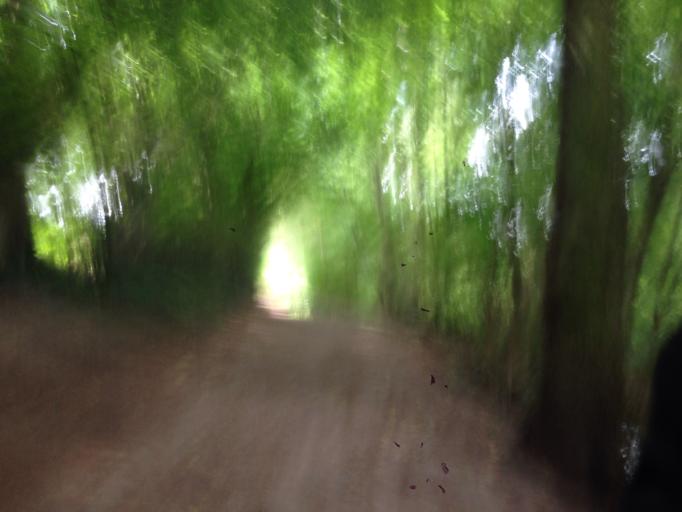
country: DE
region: Hamburg
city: Farmsen-Berne
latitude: 53.5942
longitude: 10.1281
